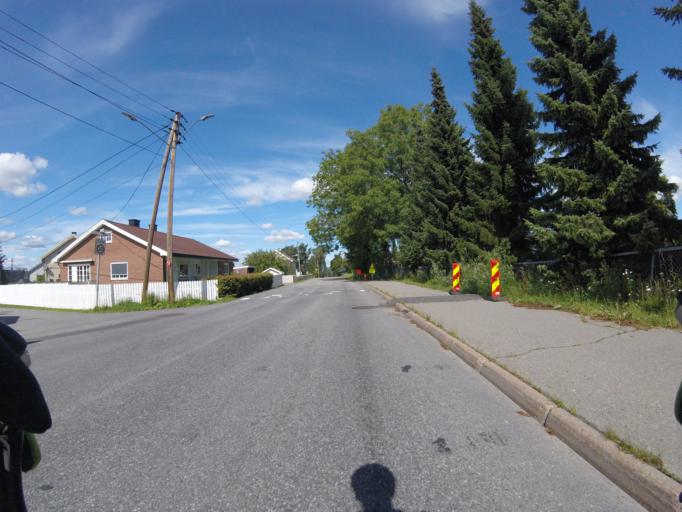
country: NO
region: Akershus
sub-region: Skedsmo
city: Lillestrom
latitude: 59.9464
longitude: 11.0203
